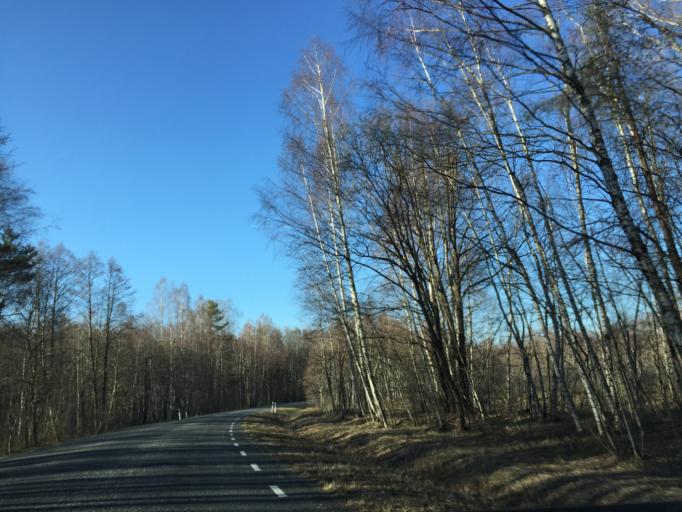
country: RU
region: Pskov
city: Gdov
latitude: 59.0247
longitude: 27.6864
